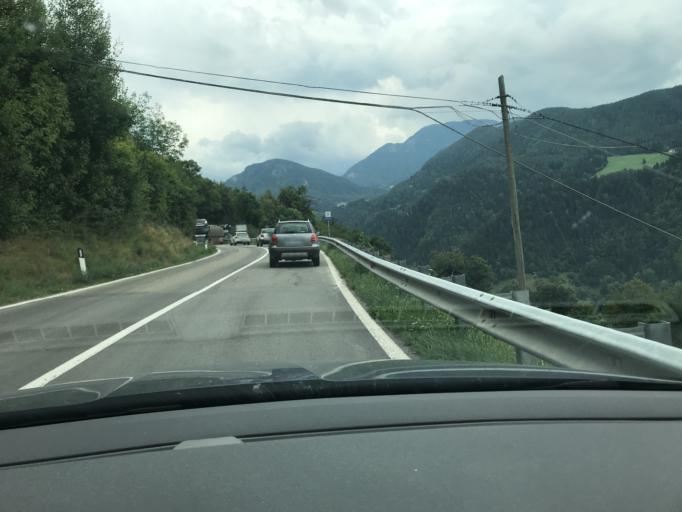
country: IT
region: Trentino-Alto Adige
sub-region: Bolzano
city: Laion
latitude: 46.6038
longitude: 11.5481
